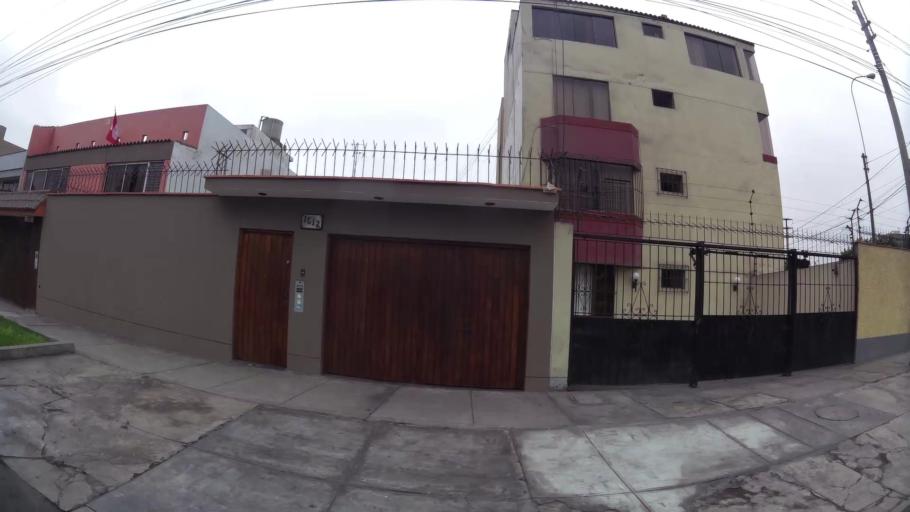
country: PE
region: Lima
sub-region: Lima
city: Surco
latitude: -12.1231
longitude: -76.9859
